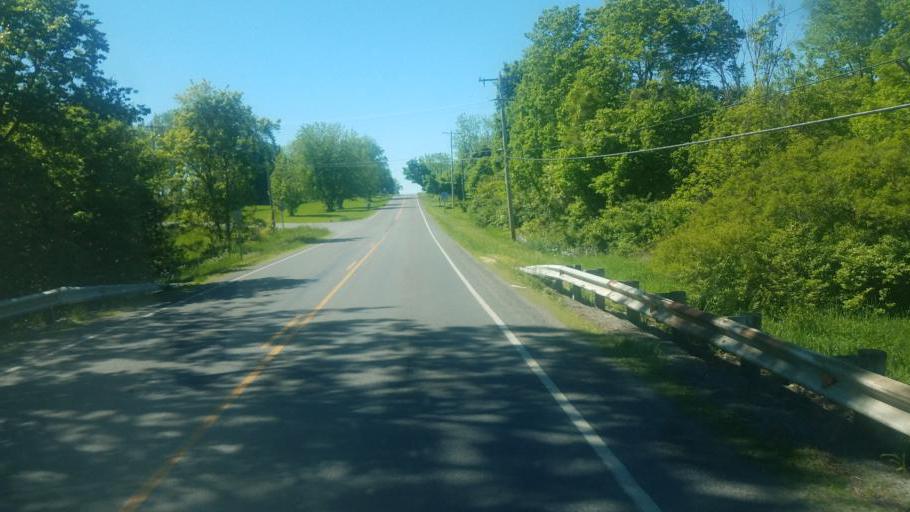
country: US
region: Ohio
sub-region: Logan County
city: Bellefontaine
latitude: 40.3845
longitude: -83.7849
